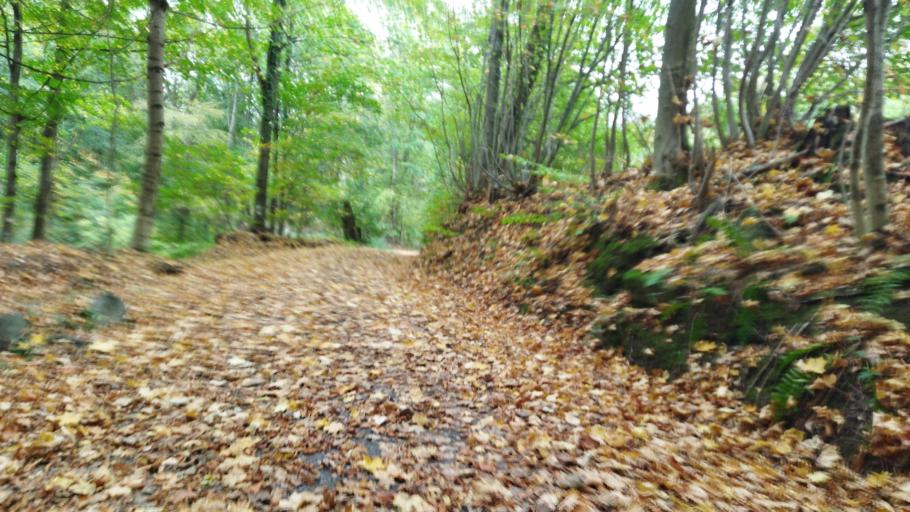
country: DE
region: Hesse
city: Lutzelbach
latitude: 49.7040
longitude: 8.7173
